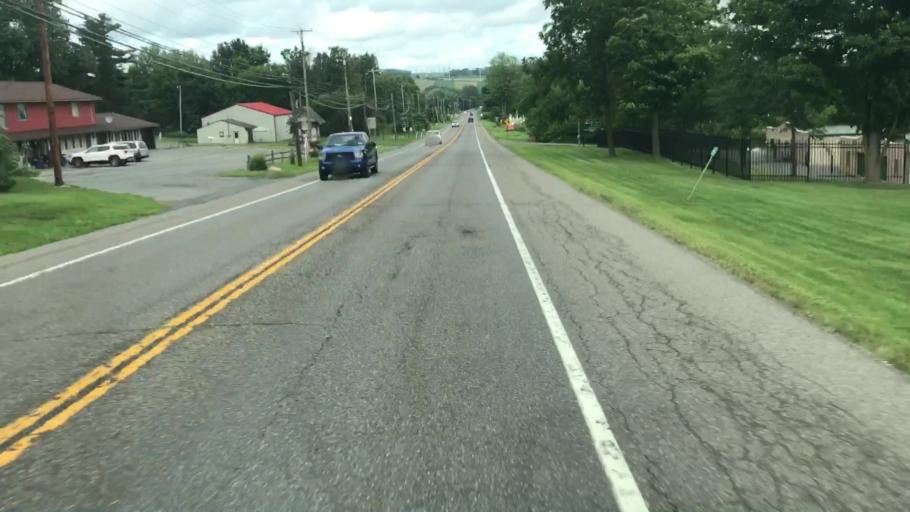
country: US
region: New York
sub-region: Onondaga County
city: Elbridge
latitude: 43.0380
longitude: -76.4234
